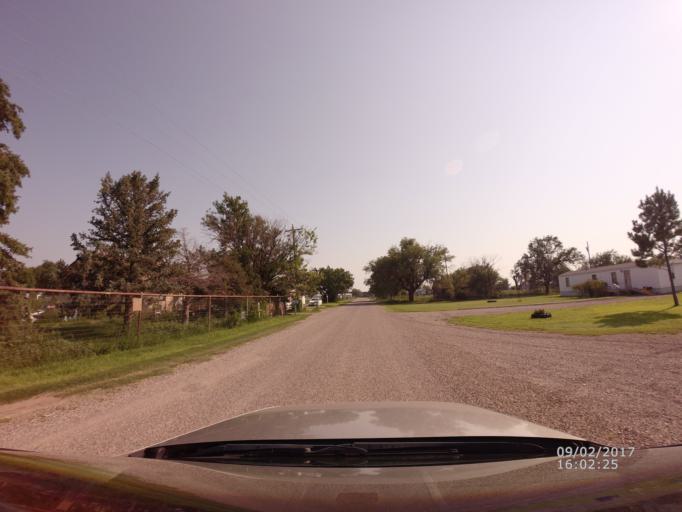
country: US
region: New Mexico
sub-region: Curry County
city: Clovis
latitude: 34.4465
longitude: -103.1996
